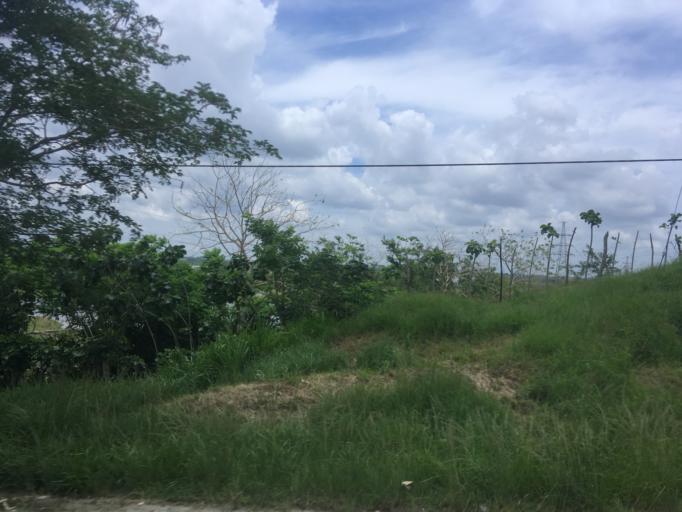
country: CU
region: Villa Clara
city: Esperanza
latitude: 22.4320
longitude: -80.0568
